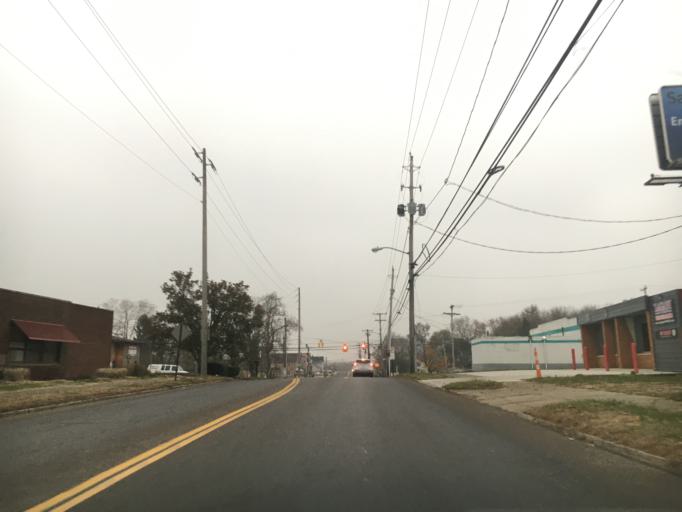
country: US
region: Ohio
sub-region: Summit County
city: Akron
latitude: 41.0954
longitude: -81.4881
